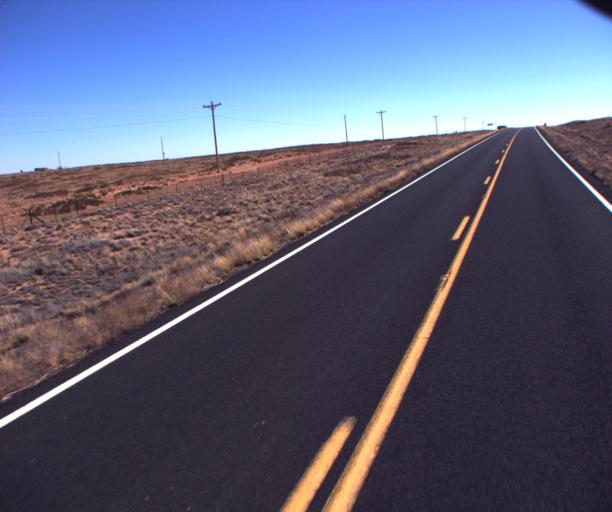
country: US
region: Arizona
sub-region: Coconino County
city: Tuba City
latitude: 36.0087
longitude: -111.0604
